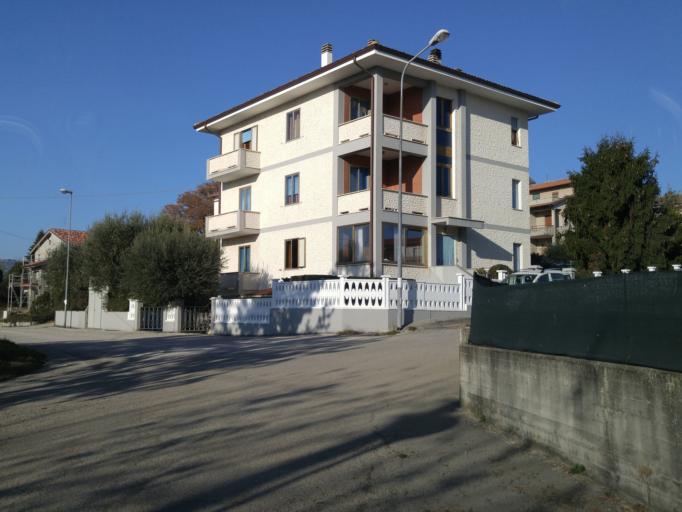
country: IT
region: The Marches
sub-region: Provincia di Pesaro e Urbino
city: Montefelcino
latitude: 43.7368
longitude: 12.8350
